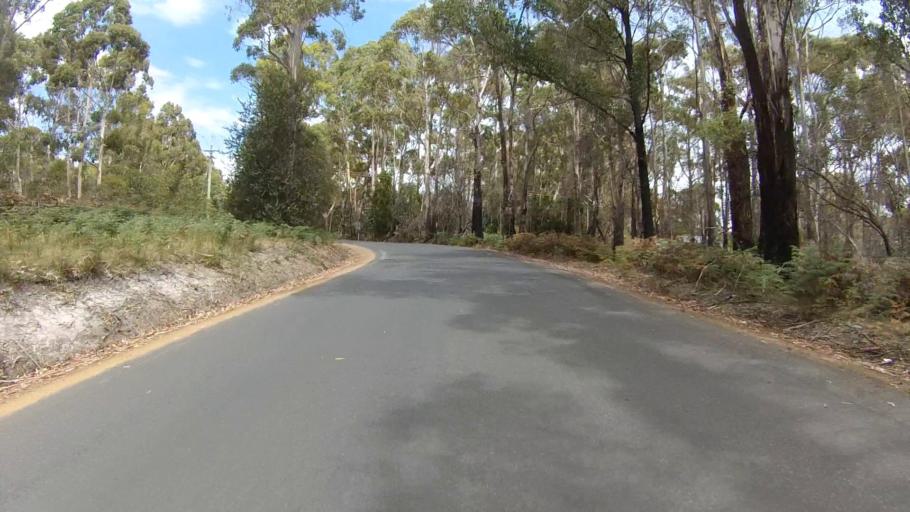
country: AU
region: Tasmania
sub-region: Kingborough
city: Blackmans Bay
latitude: -43.0093
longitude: 147.2880
